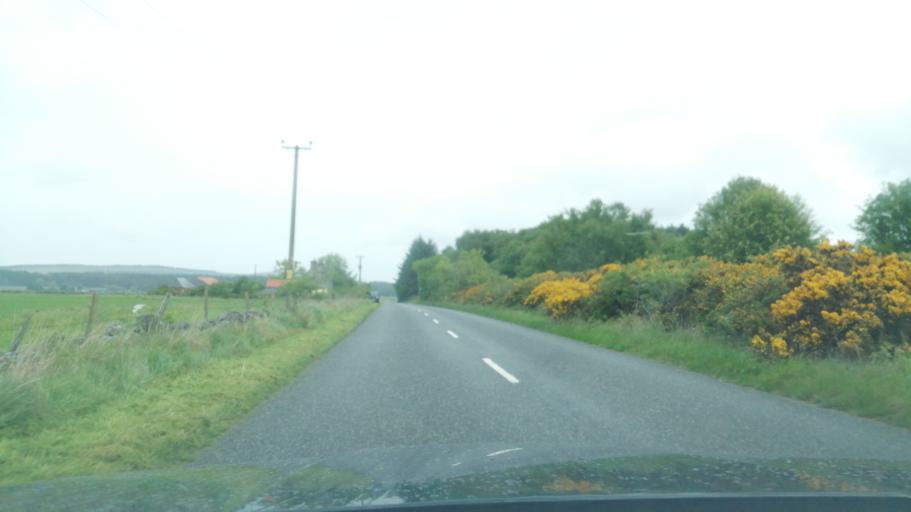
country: GB
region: Scotland
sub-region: Aberdeenshire
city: Portsoy
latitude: 57.6102
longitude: -2.7245
